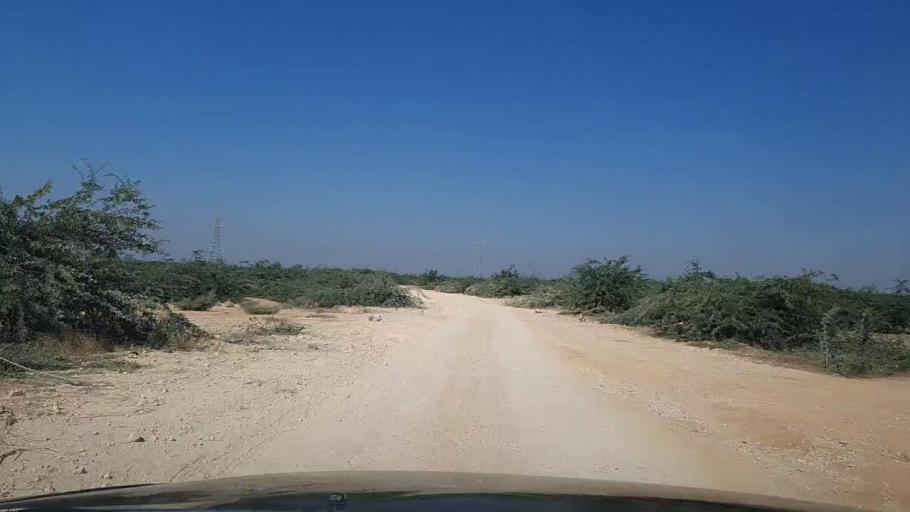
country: PK
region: Sindh
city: Thatta
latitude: 24.6233
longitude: 67.8385
